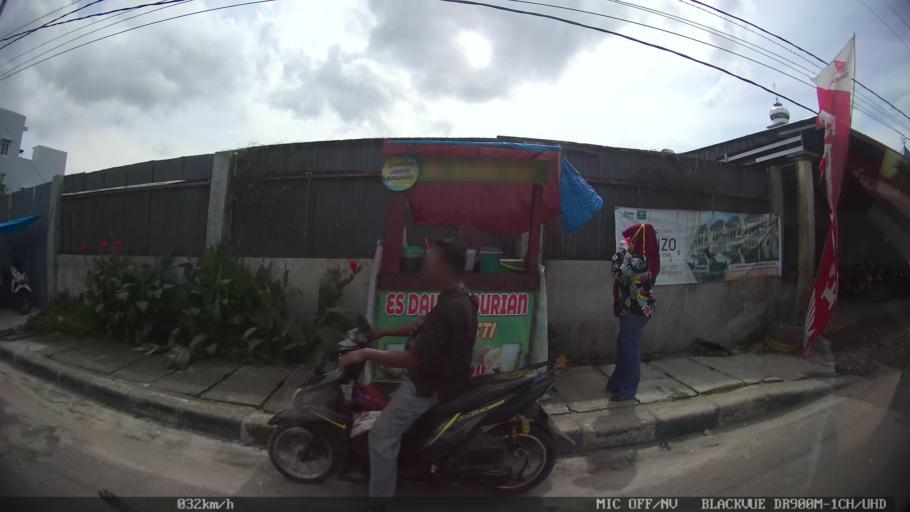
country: ID
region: North Sumatra
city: Percut
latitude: 3.5704
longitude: 98.8702
